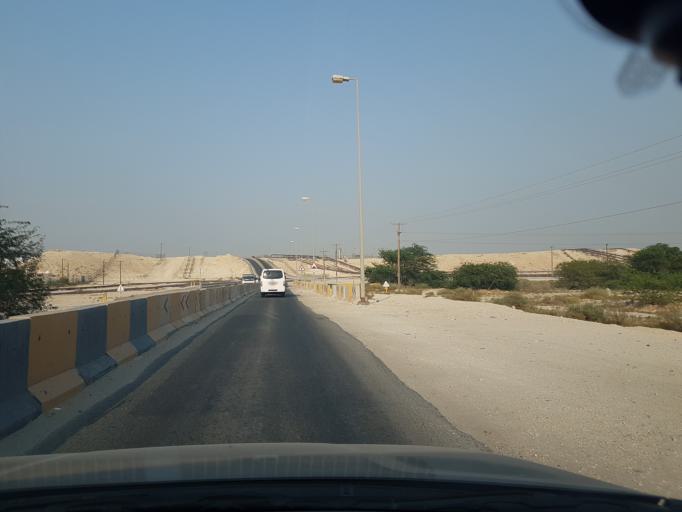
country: BH
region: Northern
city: Ar Rifa'
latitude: 26.0901
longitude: 50.5809
